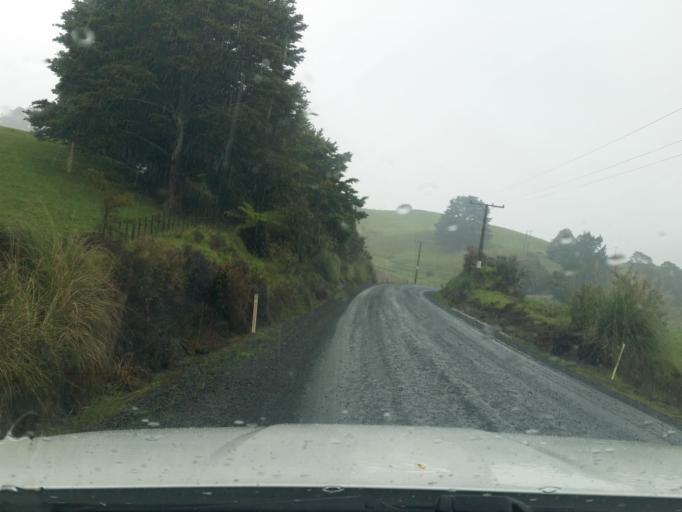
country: NZ
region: Northland
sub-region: Kaipara District
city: Dargaville
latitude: -35.8299
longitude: 174.0064
